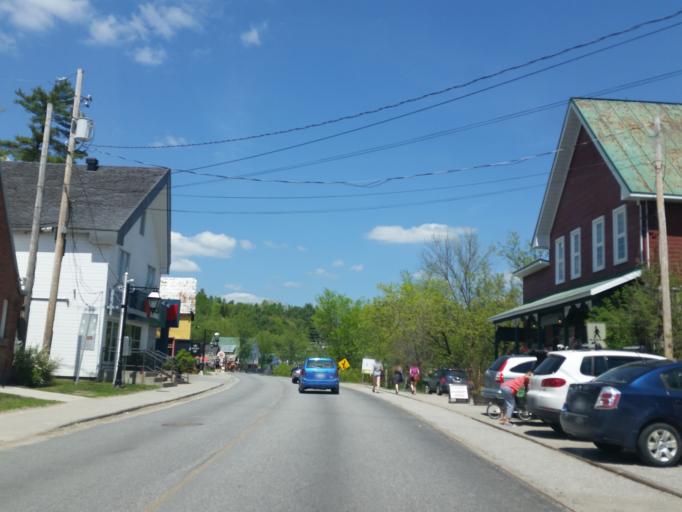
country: CA
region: Quebec
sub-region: Outaouais
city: Wakefield
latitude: 45.6346
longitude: -75.9289
